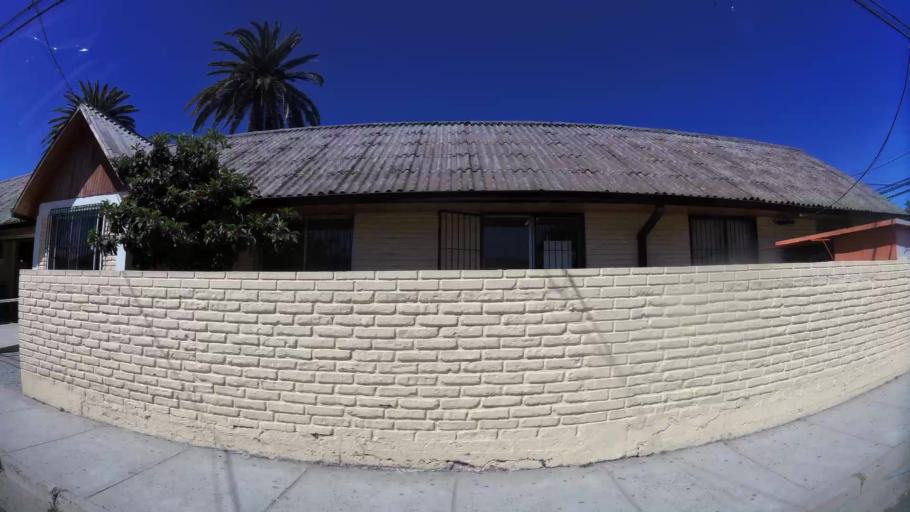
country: CL
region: Valparaiso
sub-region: Provincia de Marga Marga
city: Quilpue
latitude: -33.3188
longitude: -71.4084
